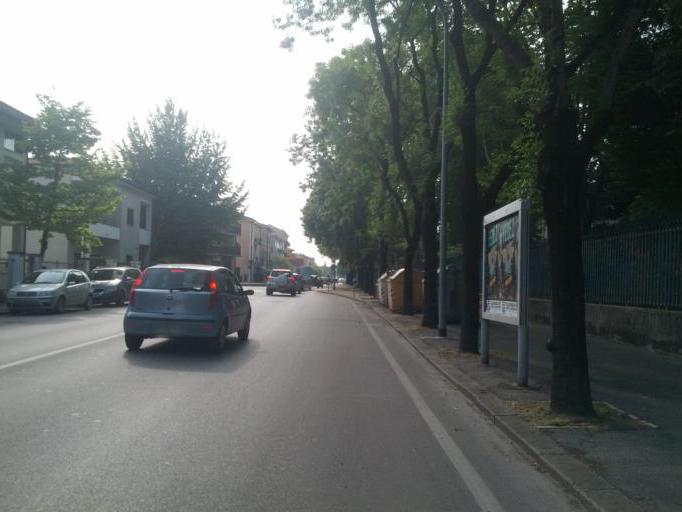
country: IT
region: Veneto
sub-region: Provincia di Verona
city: Montorio
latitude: 45.4391
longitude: 11.0376
